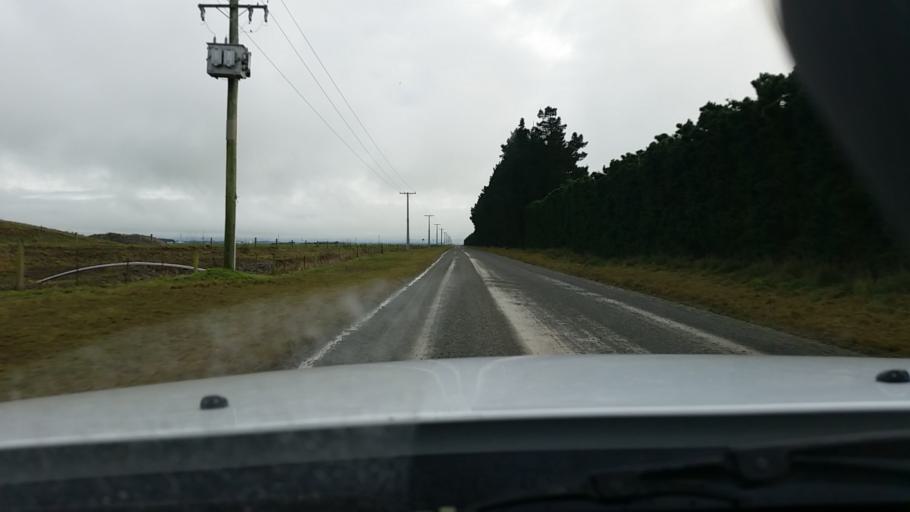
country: NZ
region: Canterbury
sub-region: Timaru District
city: Pleasant Point
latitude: -44.1046
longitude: 171.3782
